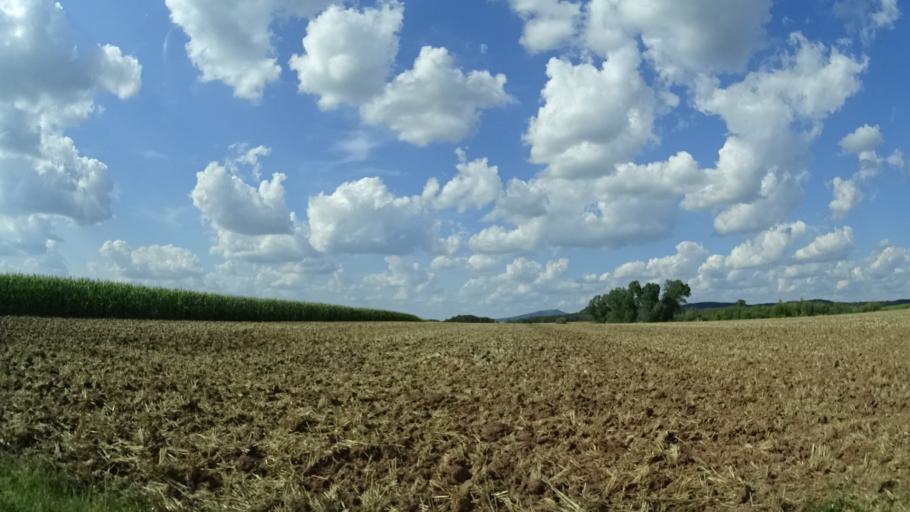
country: DE
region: Bavaria
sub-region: Regierungsbezirk Unterfranken
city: Trappstadt
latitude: 50.2857
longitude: 10.5802
